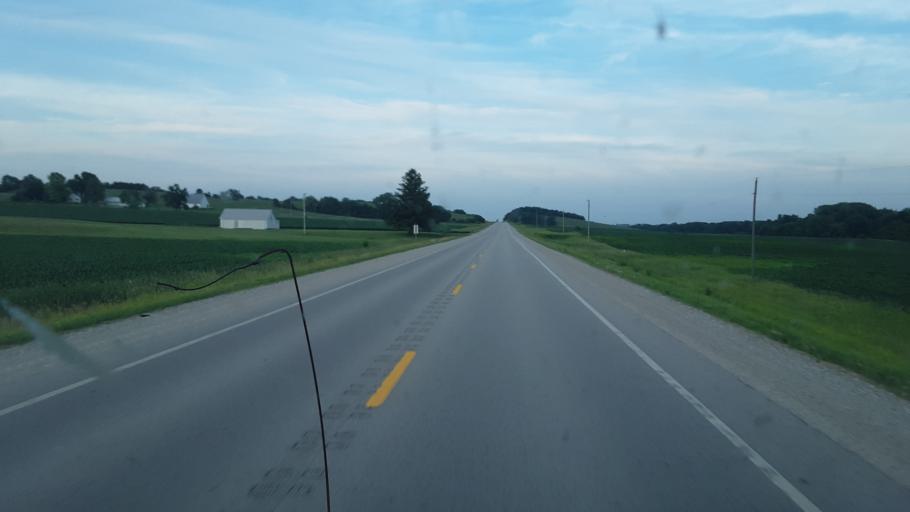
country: US
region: Iowa
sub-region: Benton County
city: Belle Plaine
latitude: 41.7427
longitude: -92.2743
